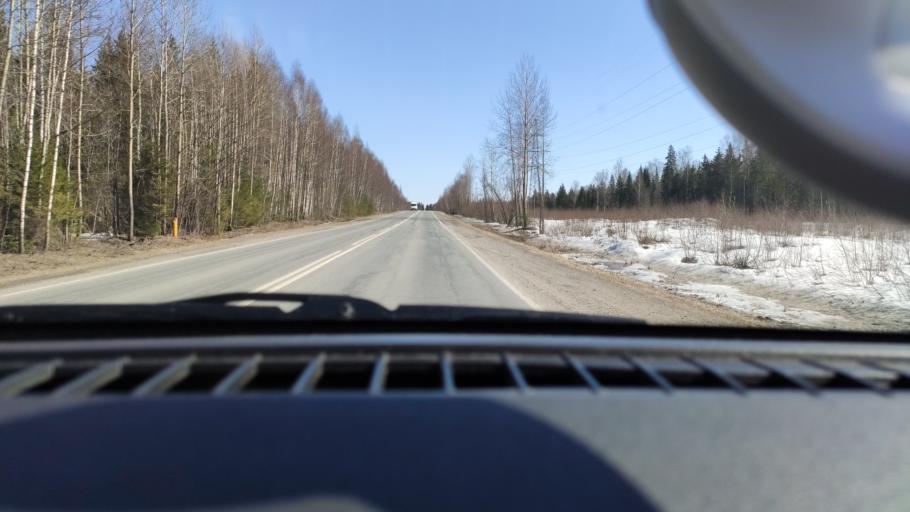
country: RU
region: Perm
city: Perm
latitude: 58.1372
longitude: 56.2837
